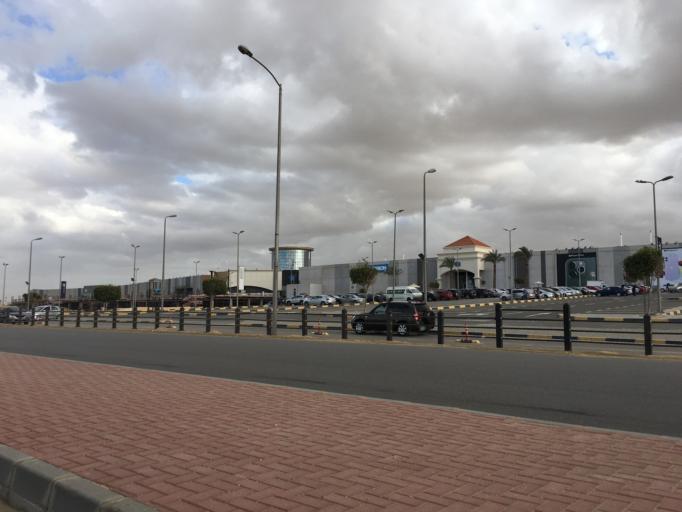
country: EG
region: Al Jizah
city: Awsim
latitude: 30.0089
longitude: 30.9725
